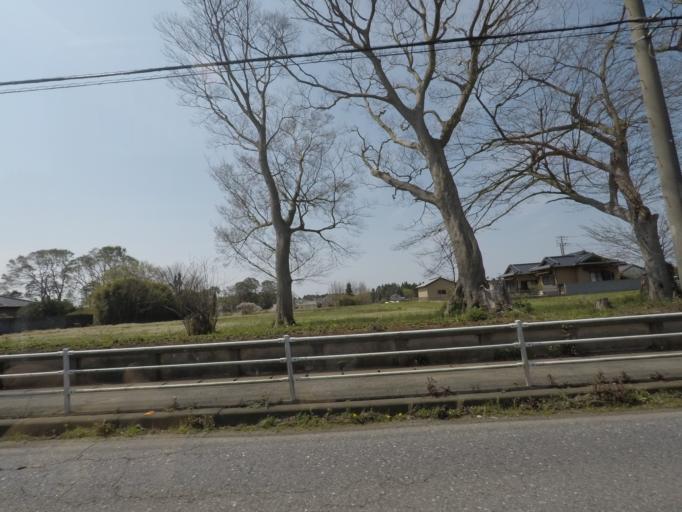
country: JP
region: Chiba
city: Narita
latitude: 35.7595
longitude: 140.3661
